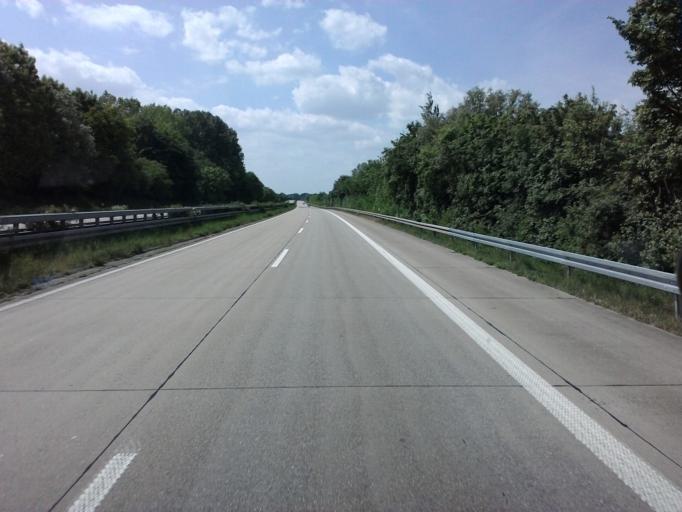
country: DE
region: North Rhine-Westphalia
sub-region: Regierungsbezirk Dusseldorf
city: Goch
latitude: 51.6745
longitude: 6.0948
